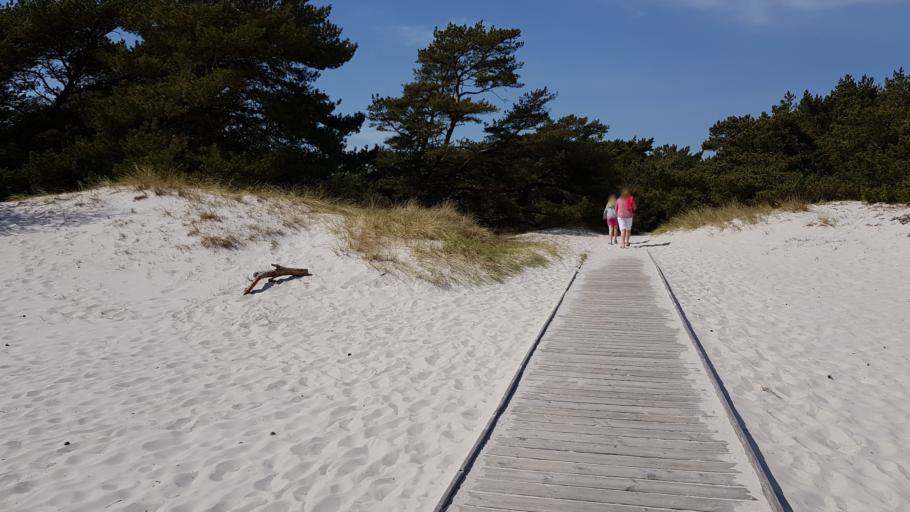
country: DK
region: Capital Region
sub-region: Bornholm Kommune
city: Nexo
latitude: 54.9914
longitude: 15.0792
